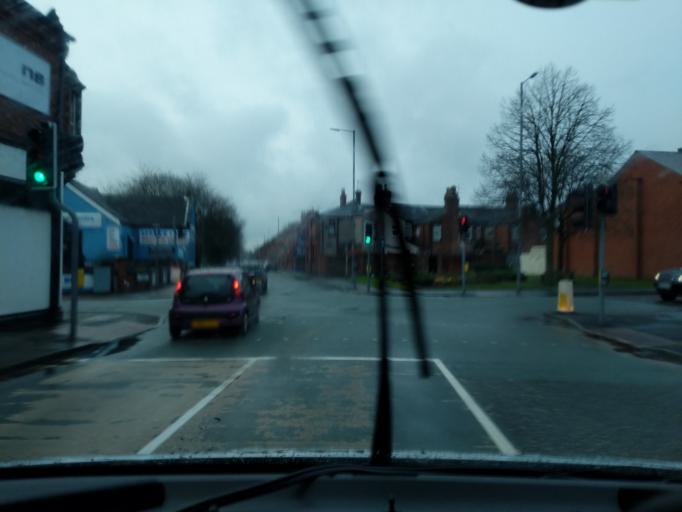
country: GB
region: England
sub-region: St. Helens
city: St Helens
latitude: 53.4558
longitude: -2.7472
